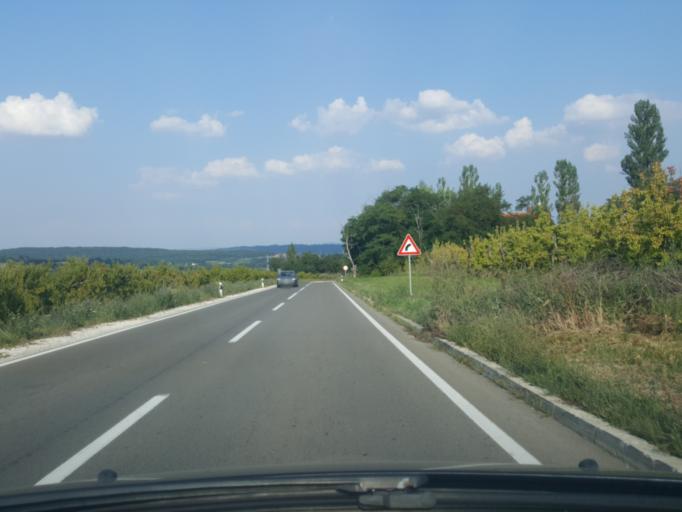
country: RS
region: Central Serbia
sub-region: Sumadijski Okrug
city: Topola
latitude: 44.2278
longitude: 20.6443
